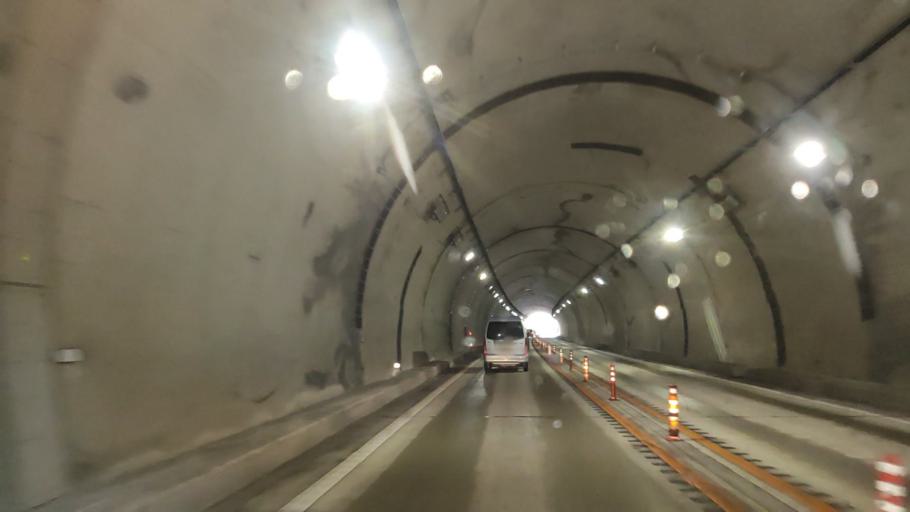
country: JP
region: Tokushima
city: Kamojimacho-jogejima
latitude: 34.1083
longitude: 134.3149
